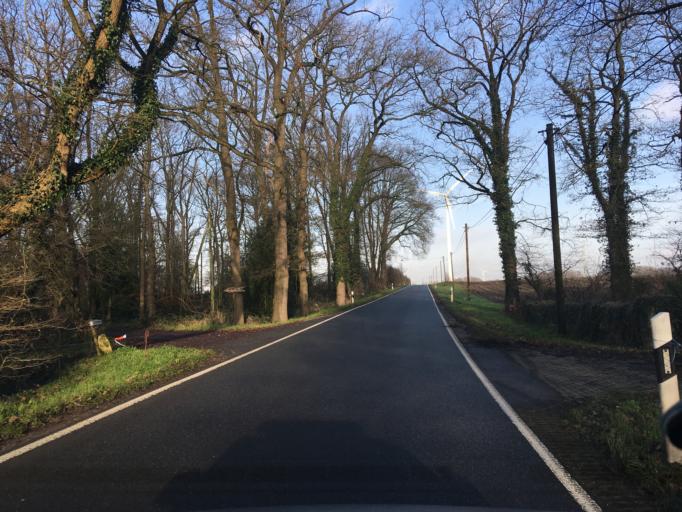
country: DE
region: North Rhine-Westphalia
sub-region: Regierungsbezirk Munster
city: Velen
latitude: 51.9203
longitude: 6.9629
